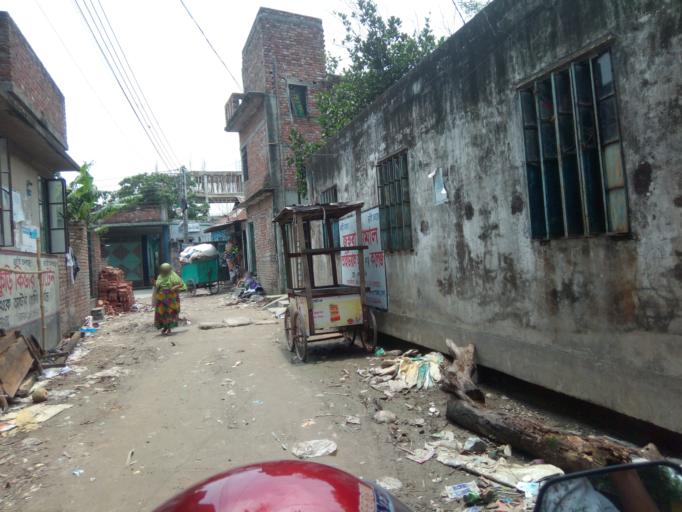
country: BD
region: Dhaka
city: Paltan
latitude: 23.7664
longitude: 90.4360
